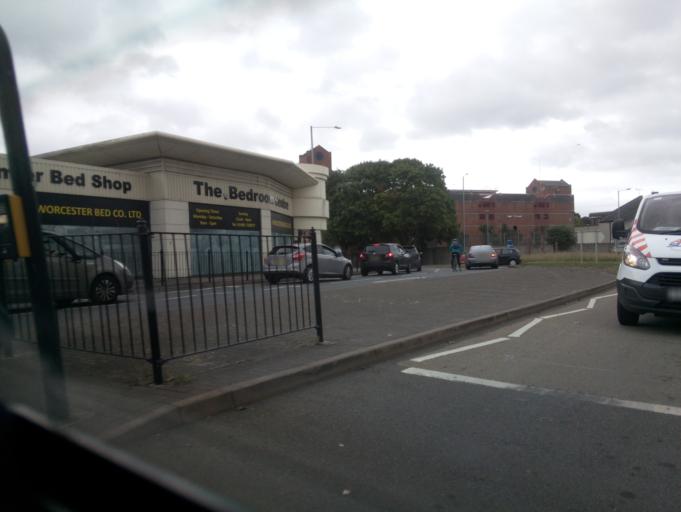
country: GB
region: England
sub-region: Worcestershire
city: Worcester
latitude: 52.1930
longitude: -2.2180
